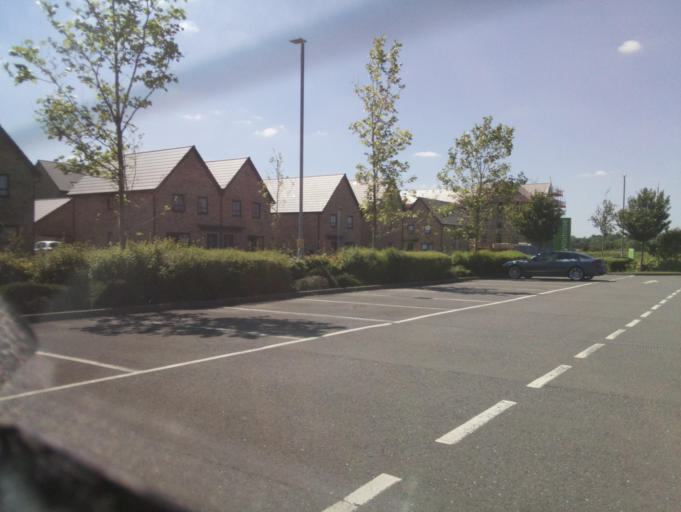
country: GB
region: England
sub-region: Borough of Swindon
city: Wroughton
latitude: 51.5438
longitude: -1.8078
